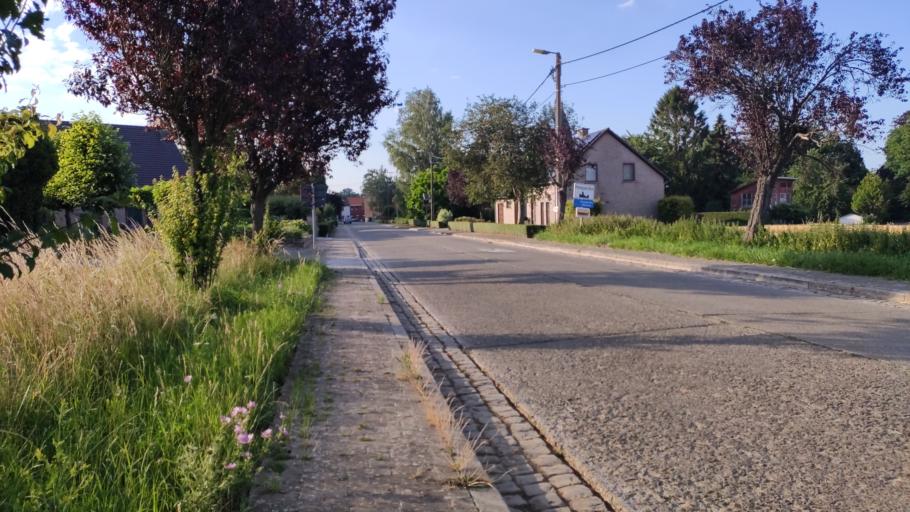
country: BE
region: Flanders
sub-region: Provincie Vlaams-Brabant
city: Hoegaarden
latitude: 50.7705
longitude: 4.8876
